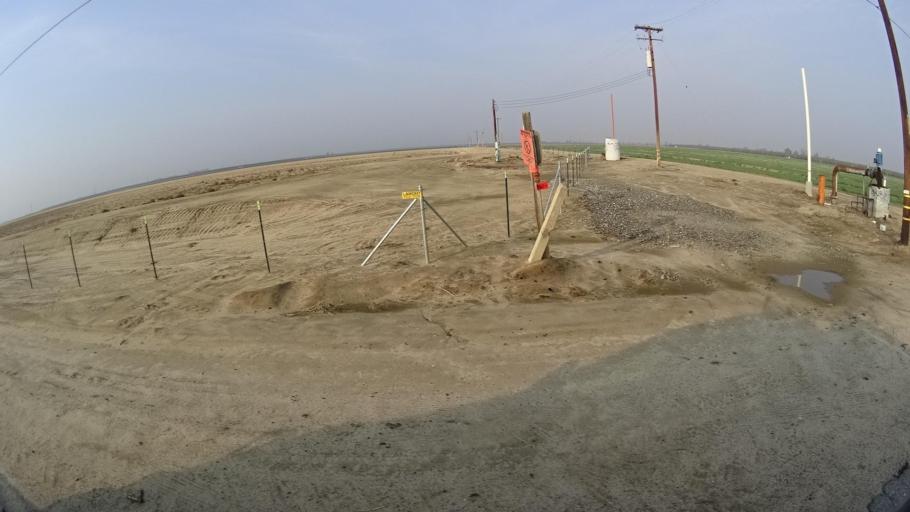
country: US
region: California
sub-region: Kern County
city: Greenfield
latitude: 35.2486
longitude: -119.0214
